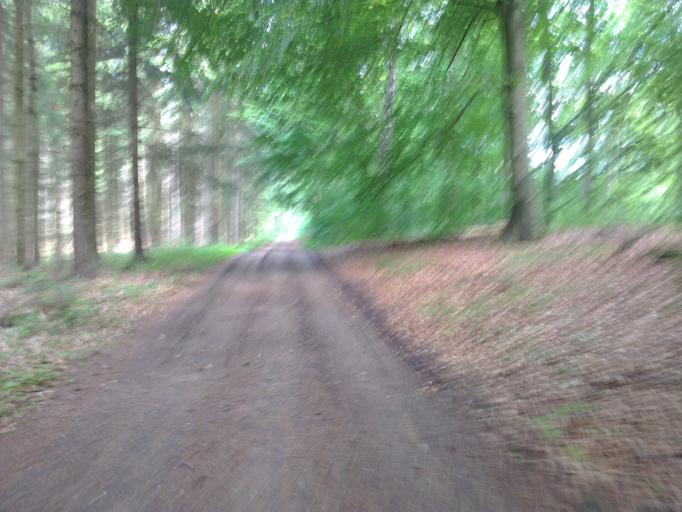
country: DK
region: Capital Region
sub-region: Halsnaes Kommune
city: Frederiksvaerk
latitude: 55.9072
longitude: 12.0114
